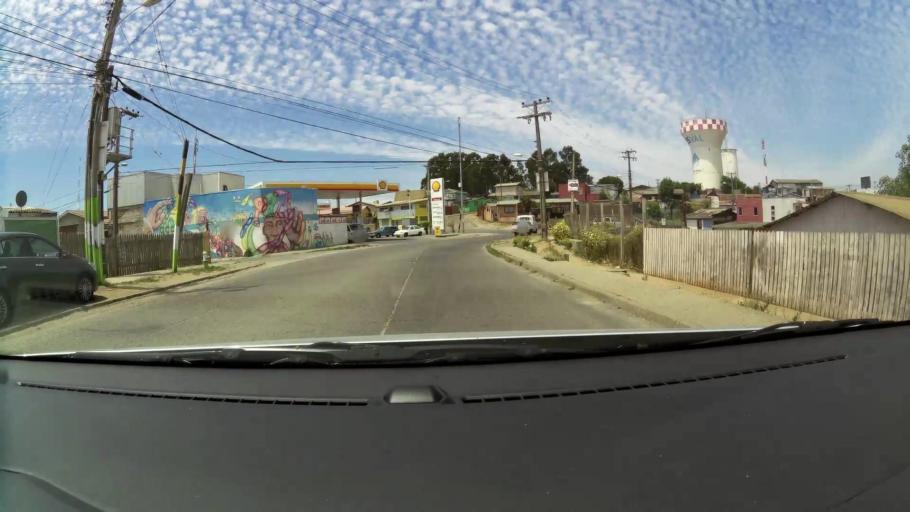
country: CL
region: Valparaiso
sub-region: Provincia de Valparaiso
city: Vina del Mar
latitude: -33.0534
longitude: -71.5603
